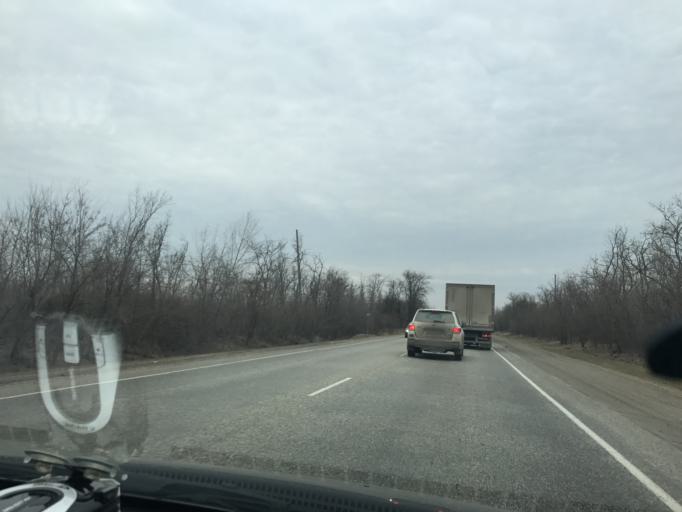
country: RU
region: Krasnodarskiy
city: Mirskoy
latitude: 45.5008
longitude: 40.4896
